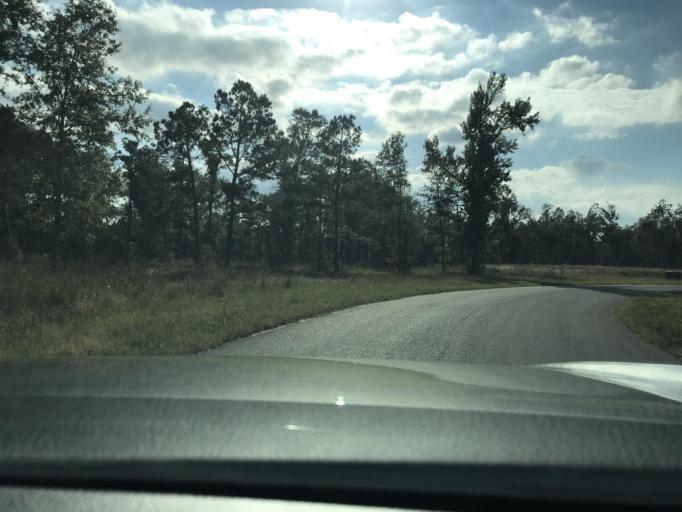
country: US
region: Louisiana
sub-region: Calcasieu Parish
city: Moss Bluff
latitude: 30.3318
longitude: -93.2484
